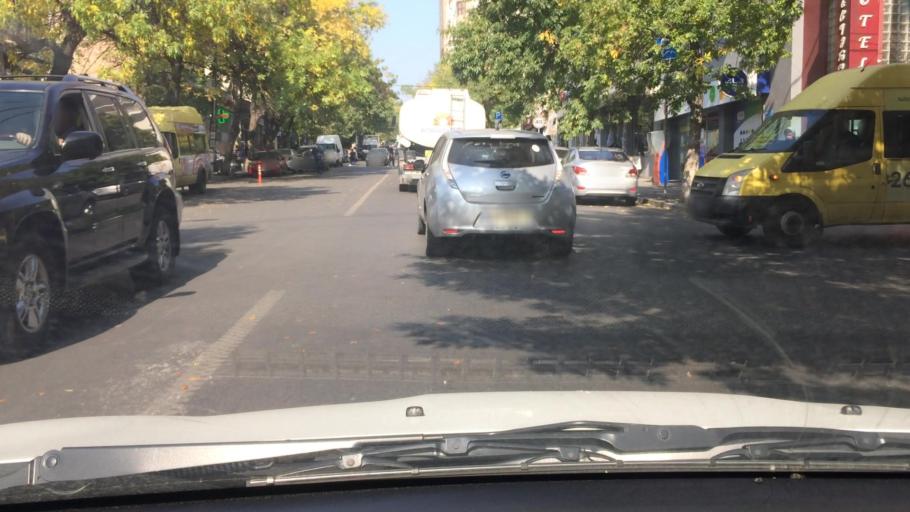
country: GE
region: T'bilisi
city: Tbilisi
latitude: 41.6881
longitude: 44.8276
